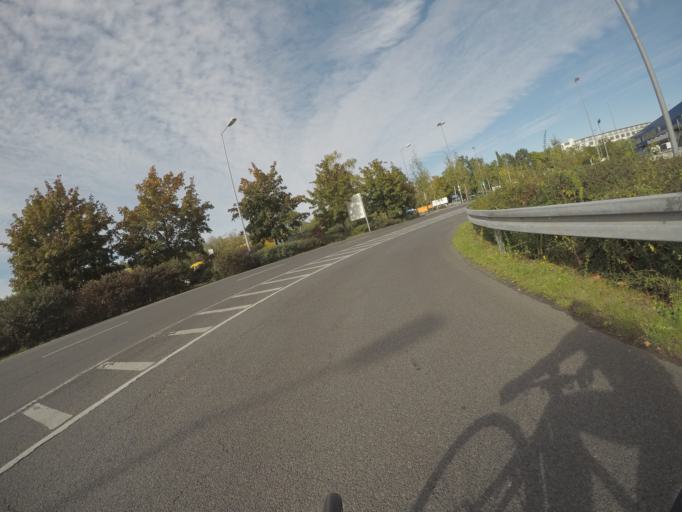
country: DE
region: Berlin
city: Schoneberg Bezirk
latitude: 52.4687
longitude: 13.3648
